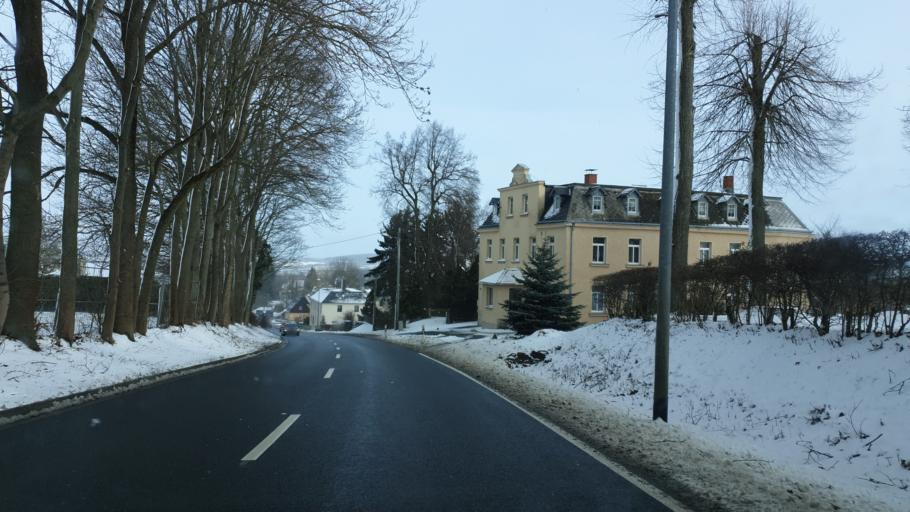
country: DE
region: Saxony
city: Oelsnitz
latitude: 50.3921
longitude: 12.1501
